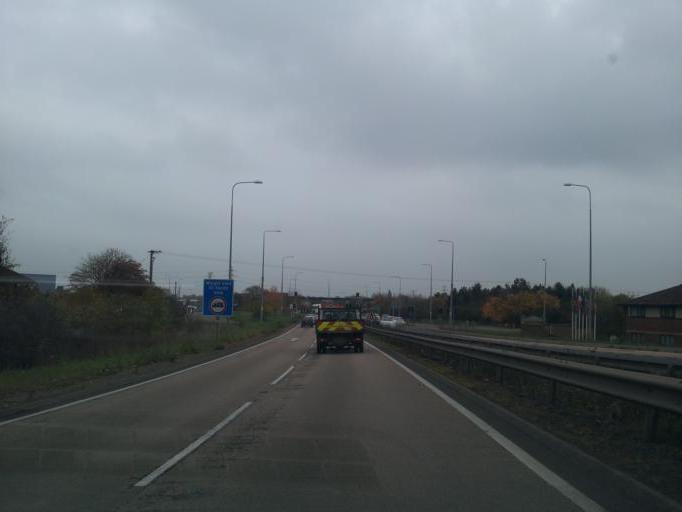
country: GB
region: England
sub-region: Cambridgeshire
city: Eaton Socon
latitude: 52.2057
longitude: -0.2930
